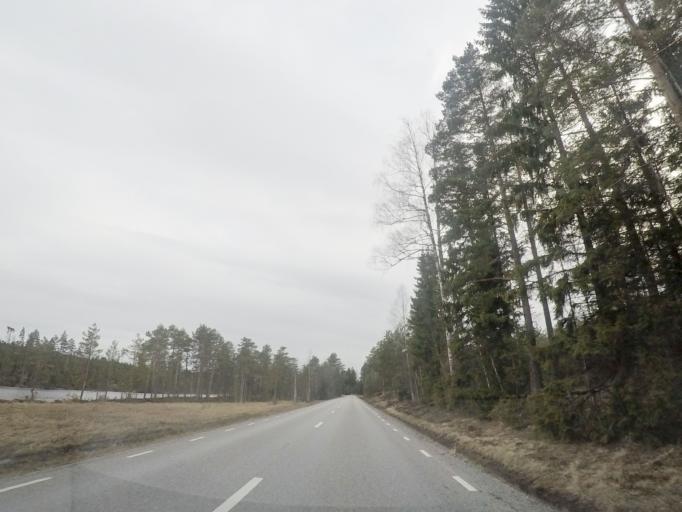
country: SE
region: OErebro
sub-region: Ljusnarsbergs Kommun
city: Kopparberg
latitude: 59.8913
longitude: 15.1675
